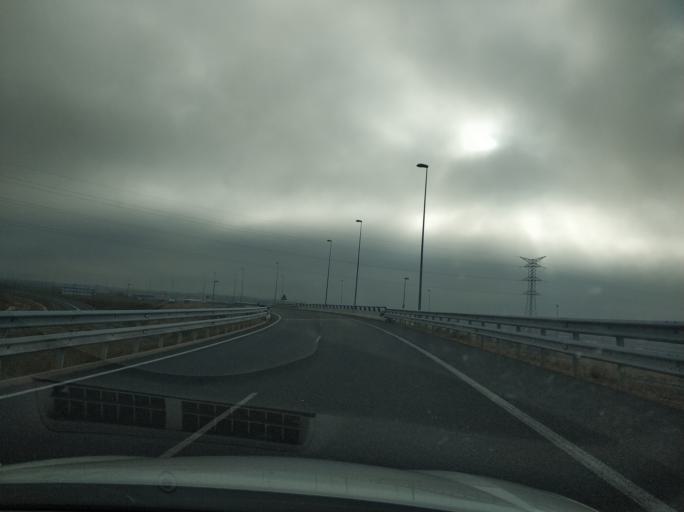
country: ES
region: Castille and Leon
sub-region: Provincia de Leon
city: Leon
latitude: 42.5707
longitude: -5.5444
